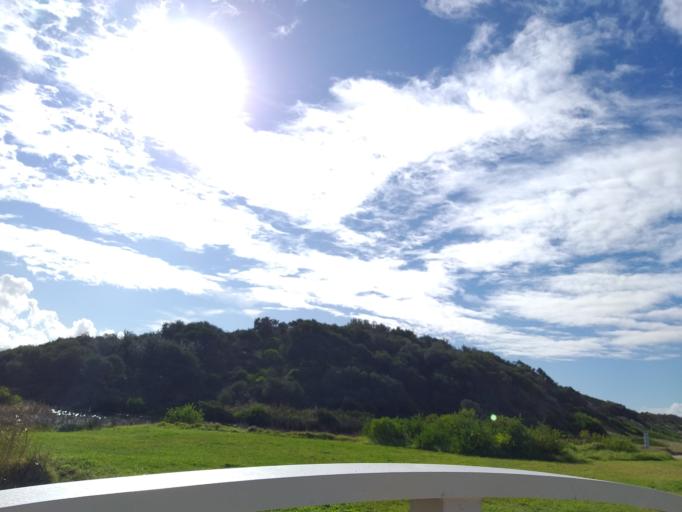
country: AU
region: New South Wales
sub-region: Wollongong
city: East Corrimal
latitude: -34.3768
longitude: 150.9197
